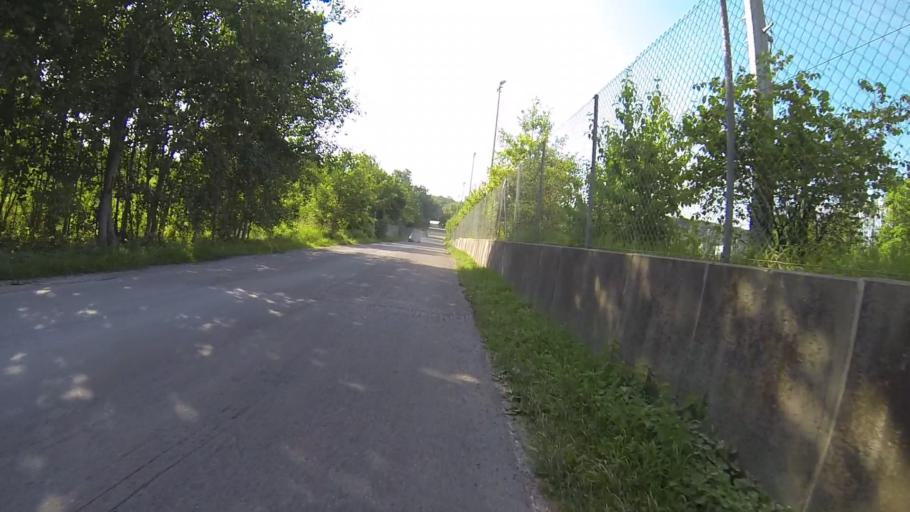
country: DE
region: Bavaria
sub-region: Swabia
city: Neu-Ulm
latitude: 48.4208
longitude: 10.0311
